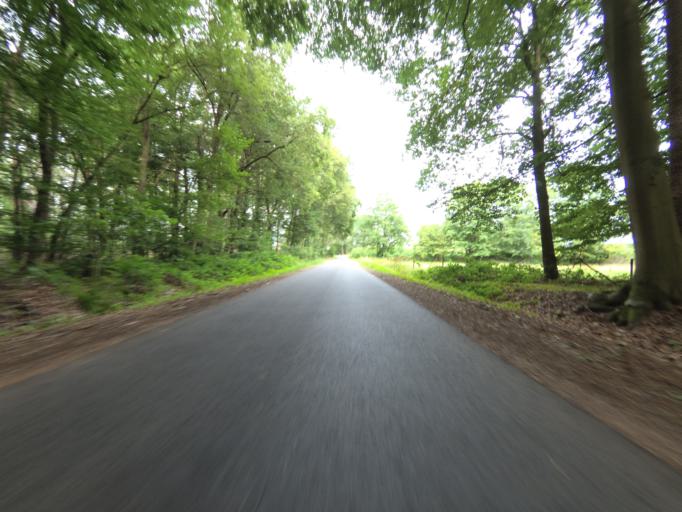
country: DE
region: North Rhine-Westphalia
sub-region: Regierungsbezirk Munster
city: Ahaus
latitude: 52.1020
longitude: 6.9986
